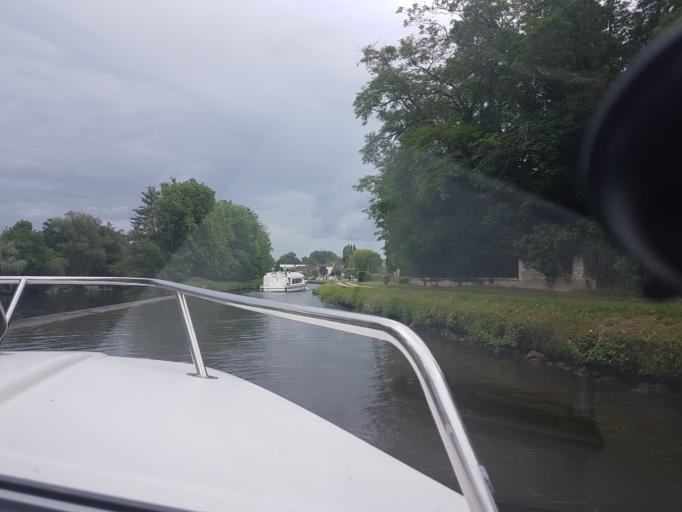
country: FR
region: Bourgogne
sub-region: Departement de l'Yonne
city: Champs-sur-Yonne
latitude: 47.7368
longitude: 3.5957
